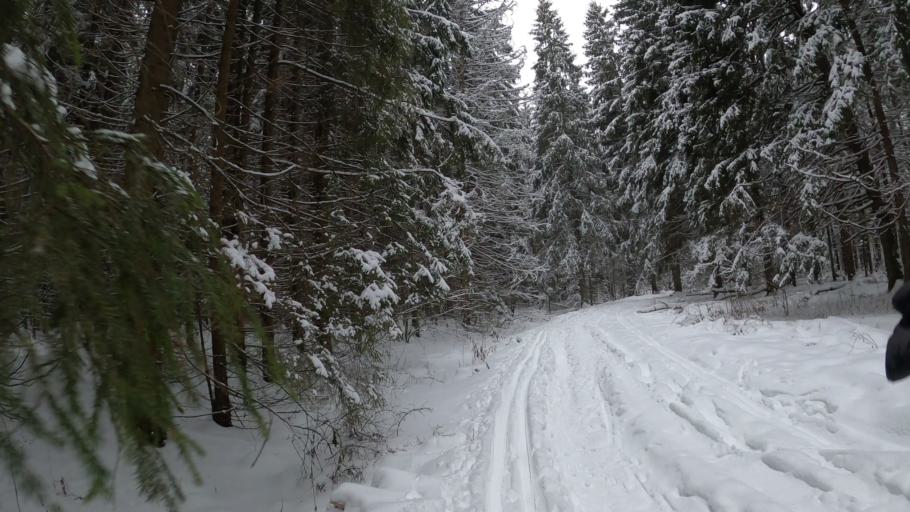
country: RU
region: Moskovskaya
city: Firsanovka
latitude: 55.9593
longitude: 37.2244
